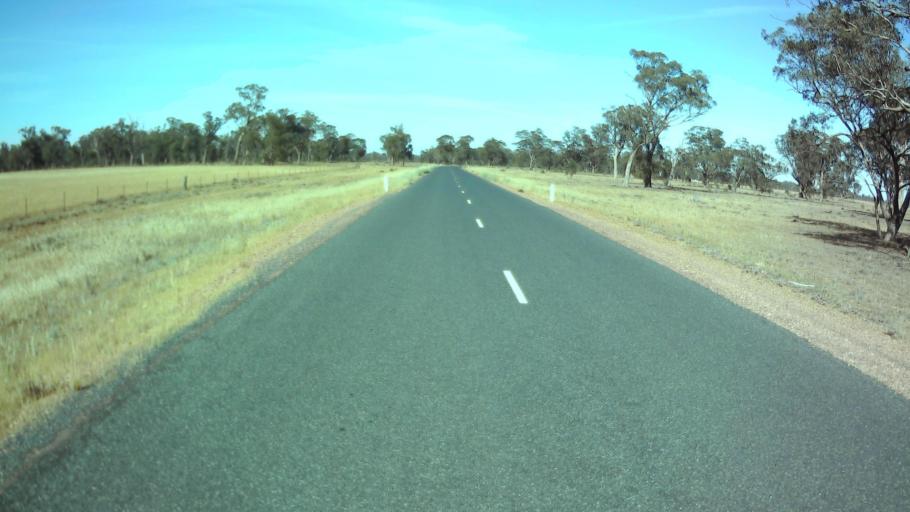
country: AU
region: New South Wales
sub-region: Weddin
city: Grenfell
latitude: -34.1109
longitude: 147.8515
